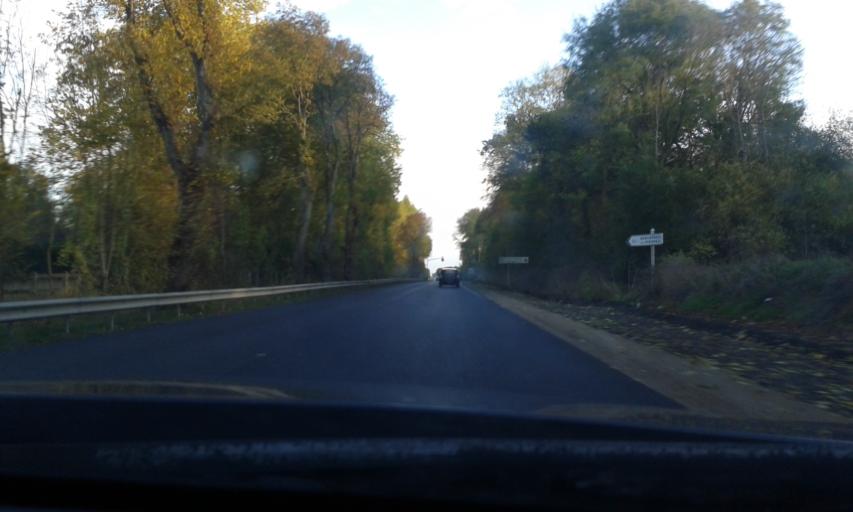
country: FR
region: Centre
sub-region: Departement d'Eure-et-Loir
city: Nogent-le-Phaye
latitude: 48.4050
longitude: 1.5484
